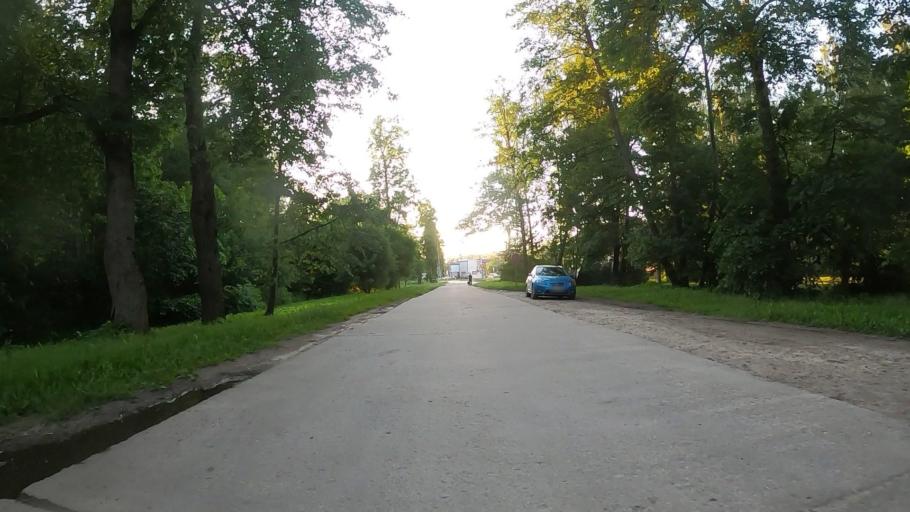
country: LV
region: Salaspils
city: Salaspils
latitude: 56.8502
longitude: 24.3354
